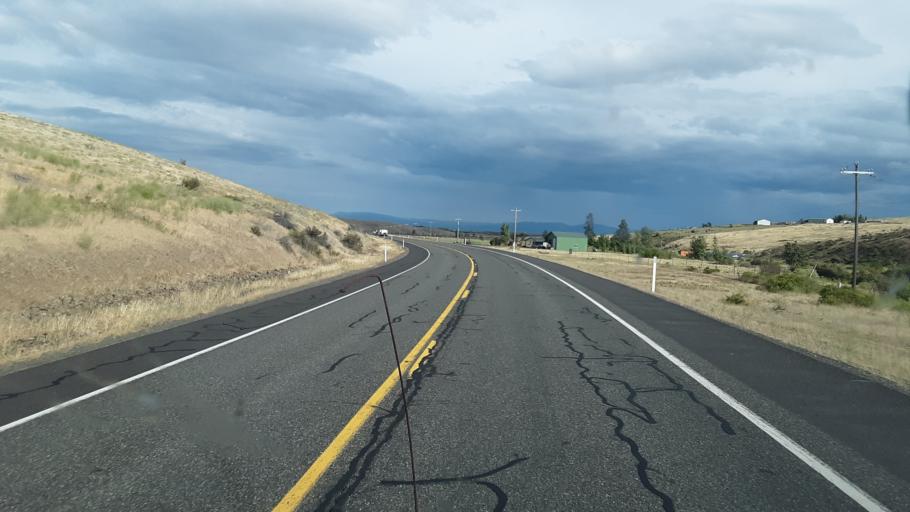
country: US
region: Washington
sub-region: Kittitas County
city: Ellensburg
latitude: 47.1283
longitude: -120.6833
